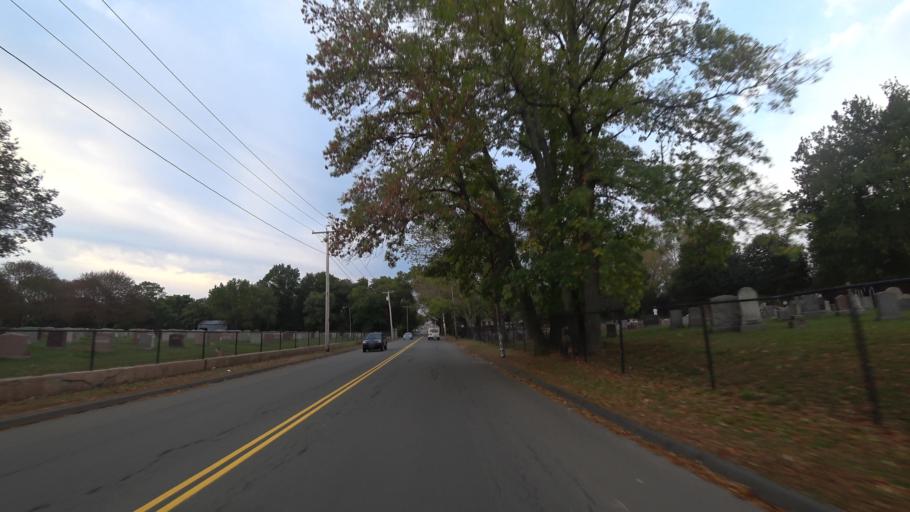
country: US
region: Massachusetts
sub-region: Middlesex County
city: Everett
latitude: 42.4263
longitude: -71.0385
